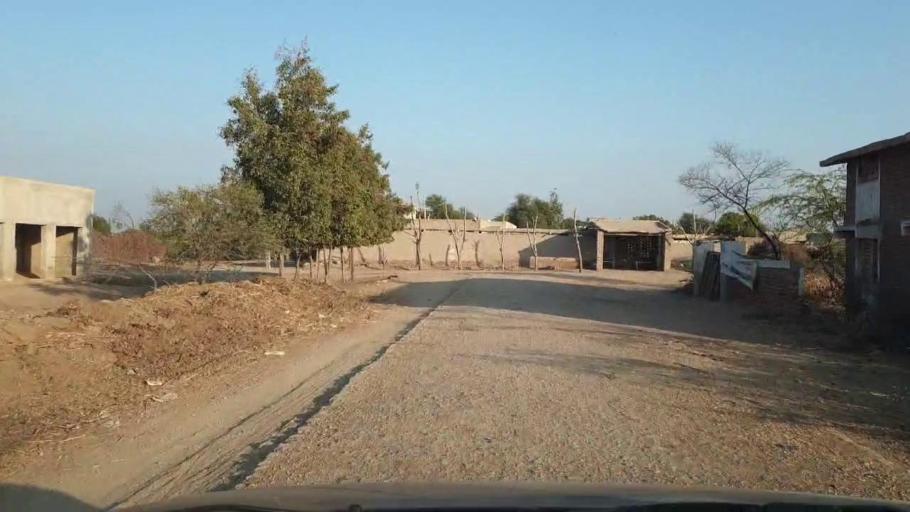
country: PK
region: Sindh
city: Digri
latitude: 25.1214
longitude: 69.2876
